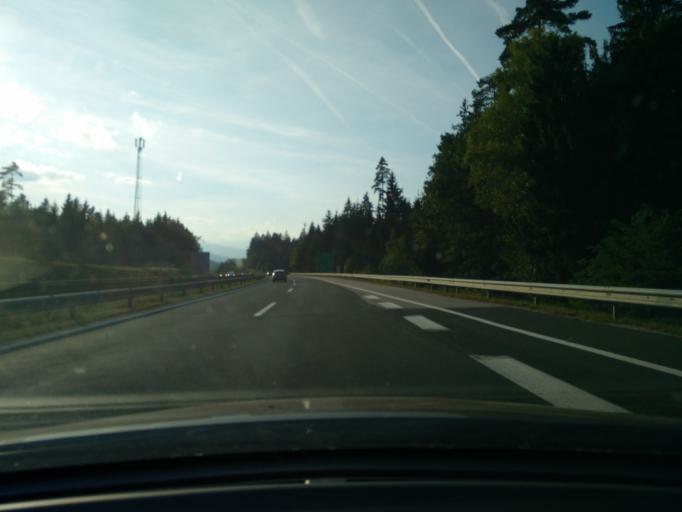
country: SI
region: Trzic
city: Bistrica pri Trzicu
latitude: 46.3126
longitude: 14.2738
